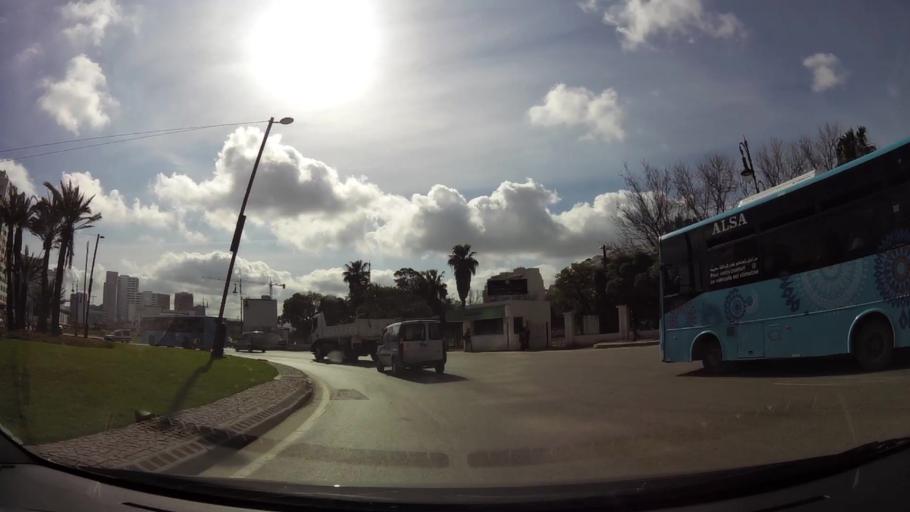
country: MA
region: Tanger-Tetouan
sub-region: Tanger-Assilah
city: Tangier
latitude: 35.7720
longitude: -5.7916
